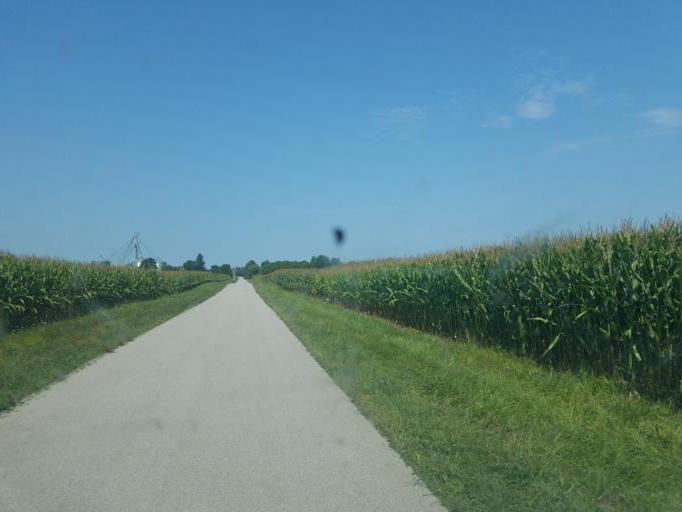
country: US
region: Ohio
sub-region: Crawford County
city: Bucyrus
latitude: 40.7837
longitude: -83.1119
